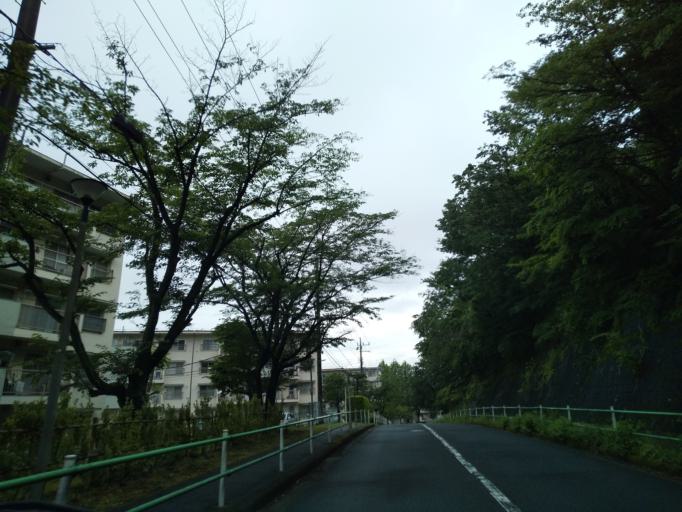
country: JP
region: Tokyo
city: Hino
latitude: 35.6509
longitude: 139.4127
